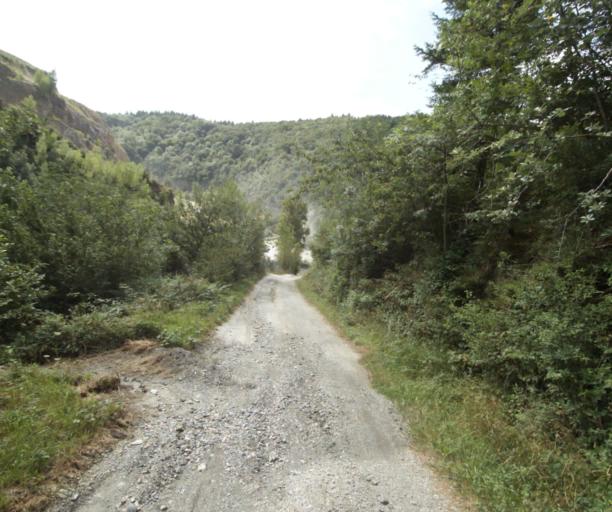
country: FR
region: Midi-Pyrenees
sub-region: Departement du Tarn
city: Soreze
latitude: 43.4561
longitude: 2.1075
